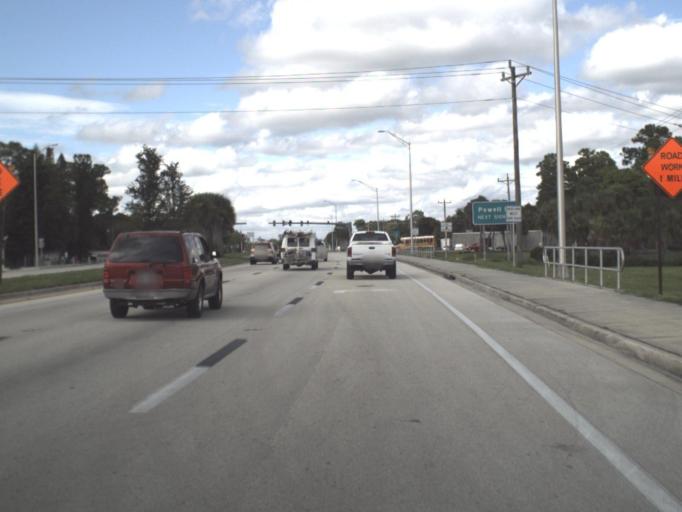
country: US
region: Florida
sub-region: Lee County
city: Palmona Park
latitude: 26.6840
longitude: -81.8840
